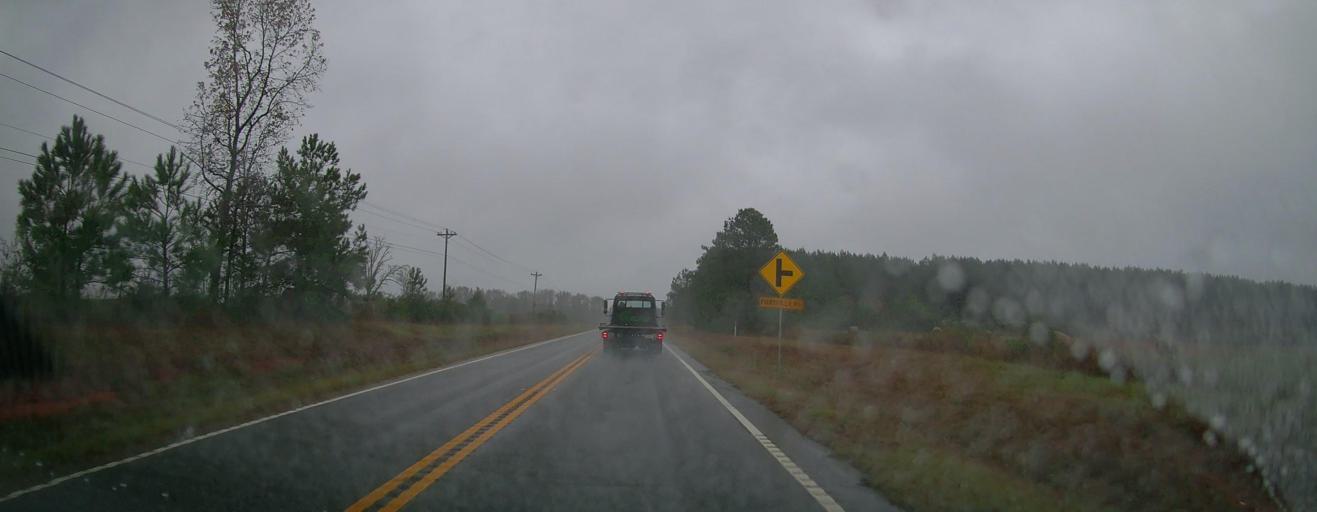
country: US
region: Georgia
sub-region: Jones County
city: Gray
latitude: 33.0544
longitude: -83.5033
